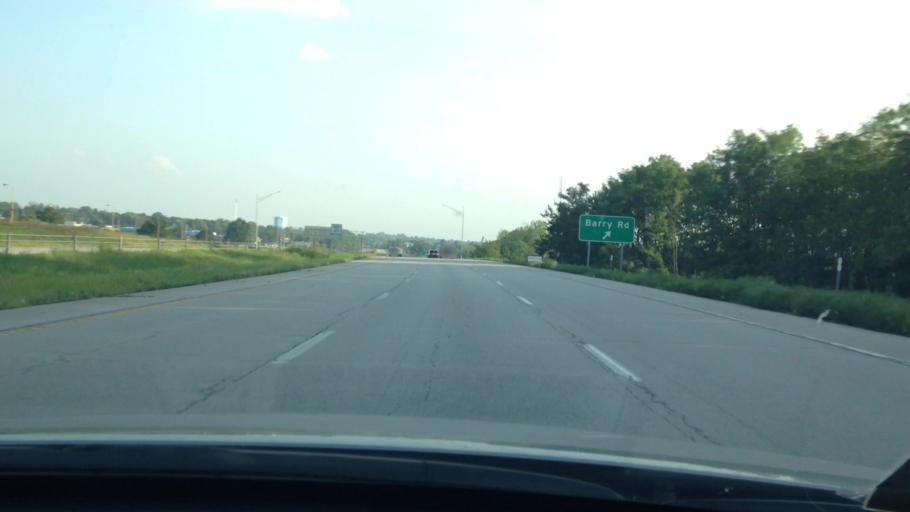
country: US
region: Missouri
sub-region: Clay County
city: Gladstone
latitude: 39.2525
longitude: -94.5904
